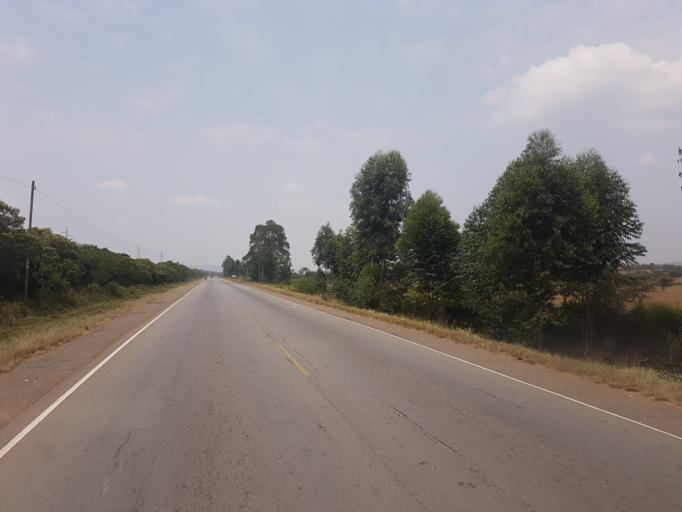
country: UG
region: Western Region
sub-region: Mbarara District
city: Mbarara
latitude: -0.5106
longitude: 30.7851
